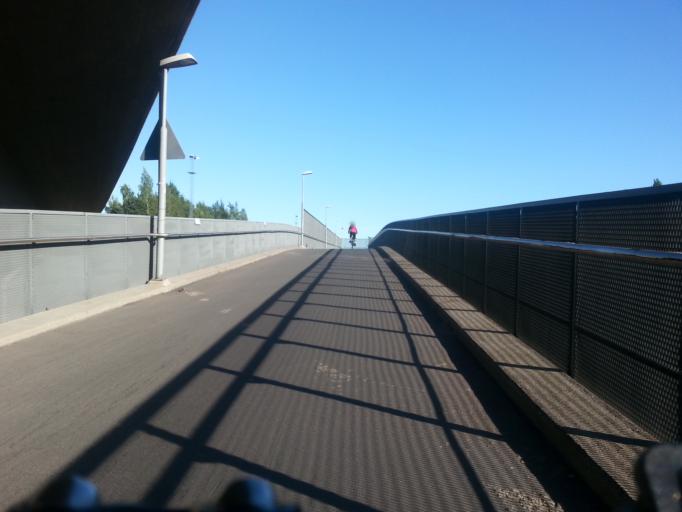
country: FI
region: Uusimaa
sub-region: Helsinki
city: Helsinki
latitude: 60.2076
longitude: 24.9217
